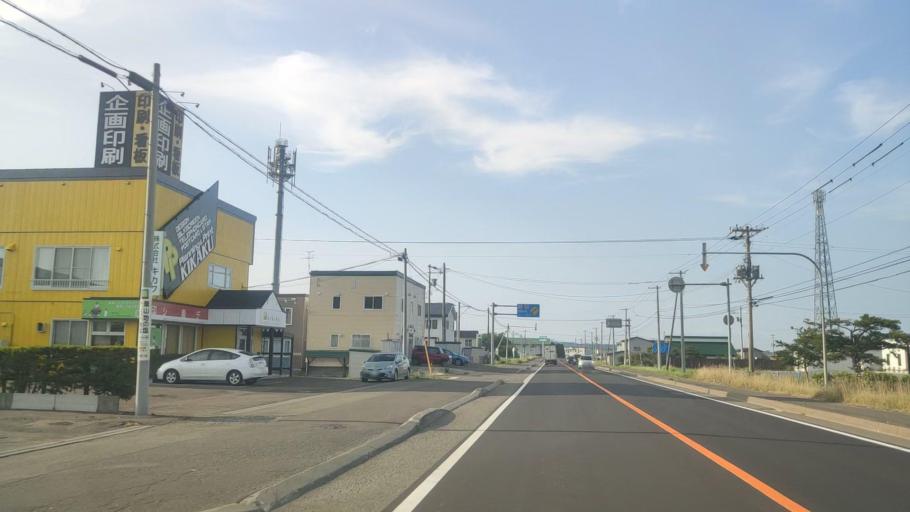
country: JP
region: Hokkaido
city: Iwamizawa
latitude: 43.0122
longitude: 141.7888
